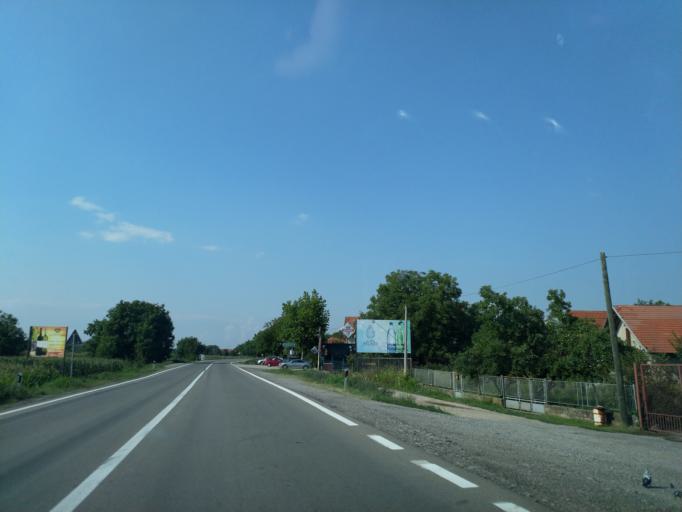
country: RS
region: Central Serbia
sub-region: Rasinski Okrug
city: Cicevac
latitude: 43.6841
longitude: 21.4123
